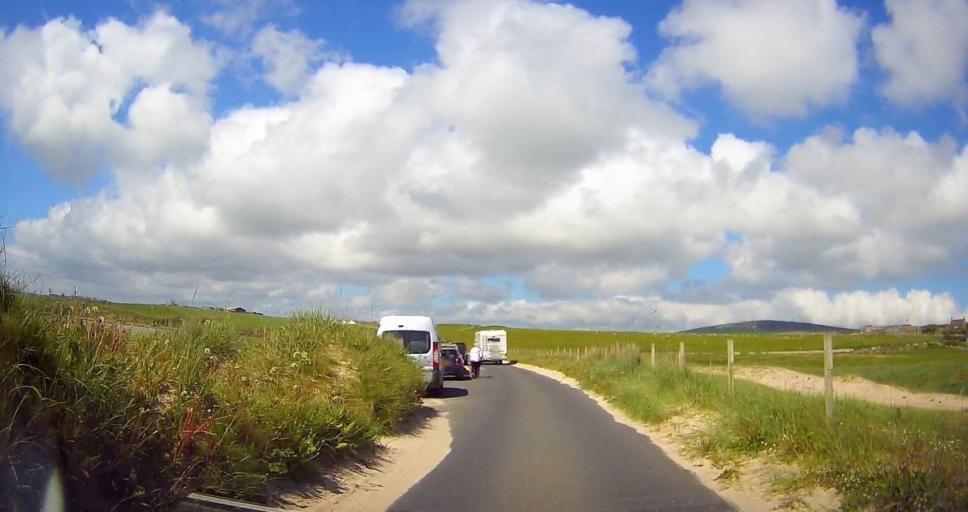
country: GB
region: Scotland
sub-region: Orkney Islands
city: Orkney
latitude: 58.9621
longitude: -2.9746
